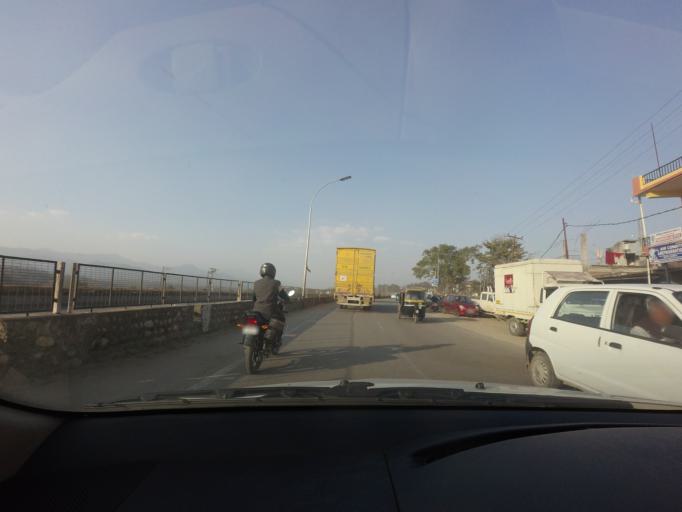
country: IN
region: Himachal Pradesh
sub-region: Mandi
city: Sundarnagar
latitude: 31.5431
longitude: 76.8972
